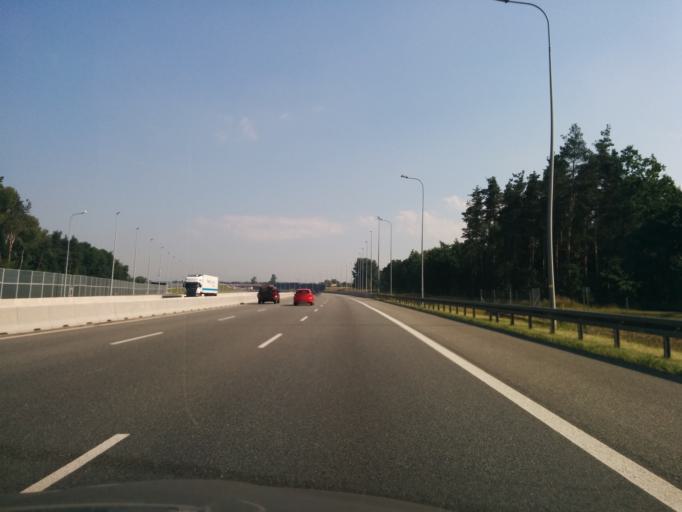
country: PL
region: Silesian Voivodeship
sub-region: Zabrze
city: Zabrze
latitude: 50.3280
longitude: 18.7298
